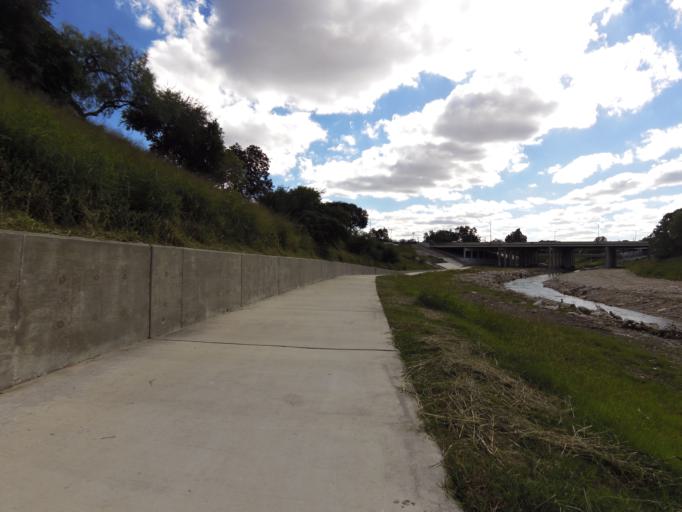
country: US
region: Texas
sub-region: Bexar County
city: San Antonio
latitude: 29.3977
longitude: -98.5013
